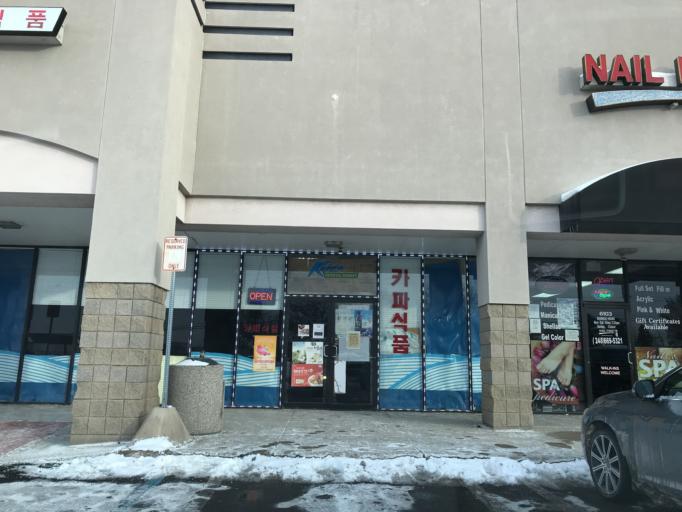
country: US
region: Michigan
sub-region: Oakland County
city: Wolverine Lake
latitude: 42.5469
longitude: -83.4379
